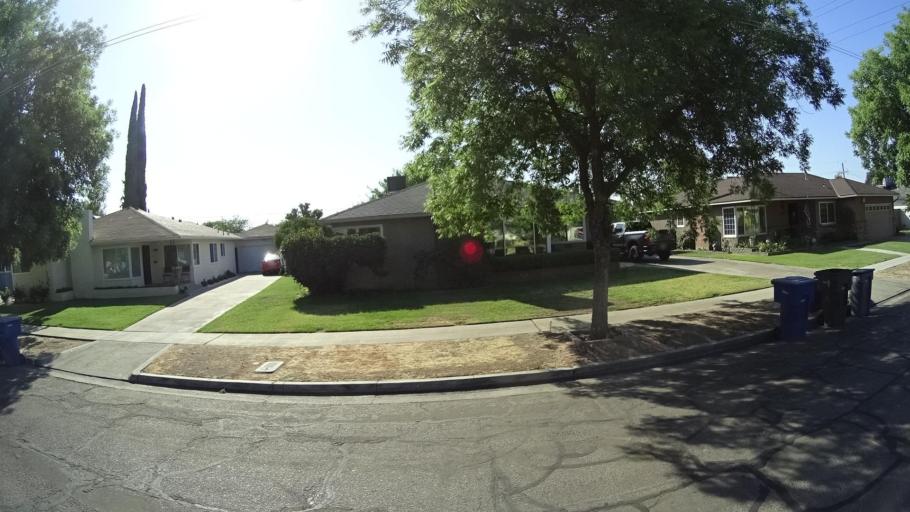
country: US
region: California
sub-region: Fresno County
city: Fresno
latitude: 36.7787
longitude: -119.7602
